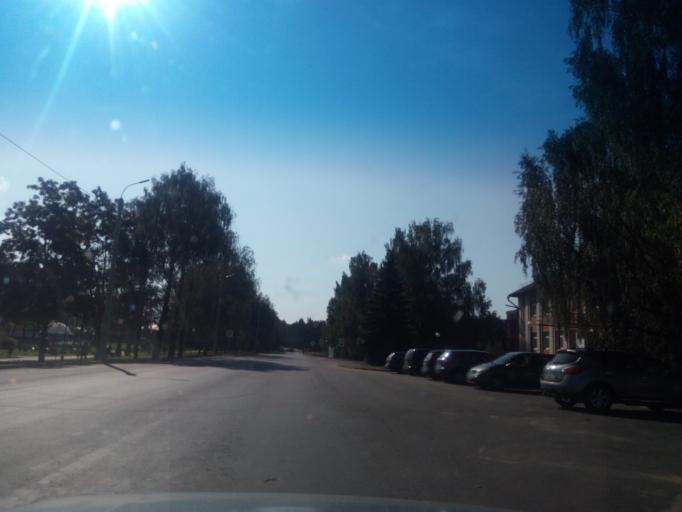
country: BY
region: Vitebsk
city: Vyerkhnyadzvinsk
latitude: 55.7626
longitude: 27.9415
